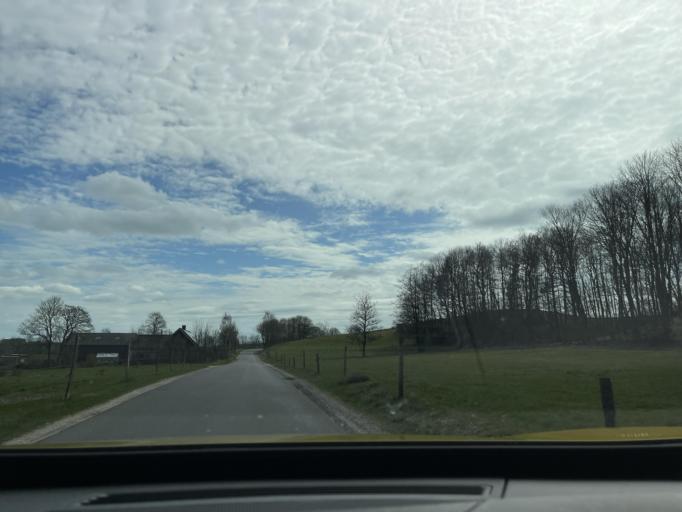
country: DK
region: Central Jutland
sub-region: Favrskov Kommune
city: Hinnerup
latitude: 56.3037
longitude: 10.0997
